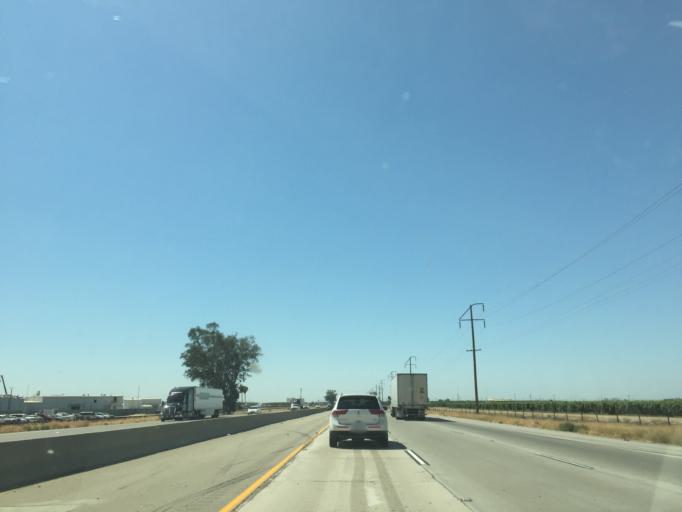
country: US
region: California
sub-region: Kern County
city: Rosedale
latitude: 35.4828
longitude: -119.1418
